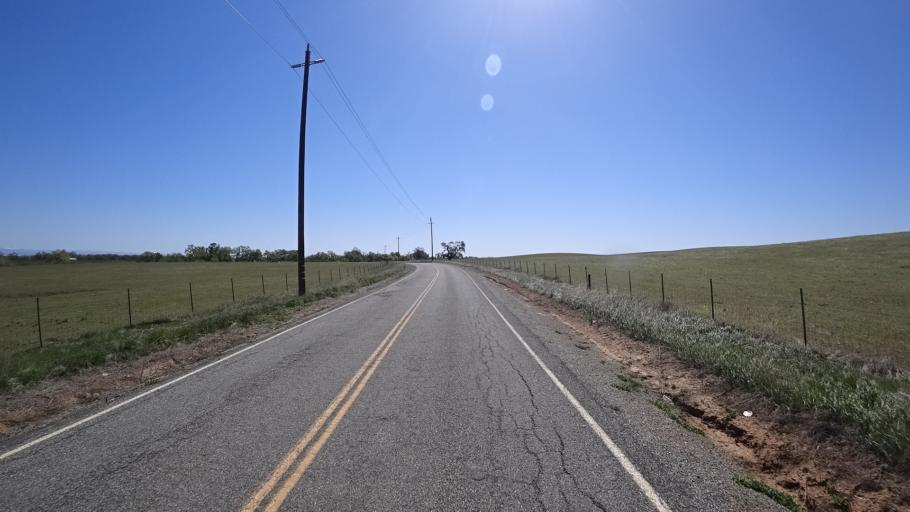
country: US
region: California
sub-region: Glenn County
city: Orland
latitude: 39.8008
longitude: -122.3232
